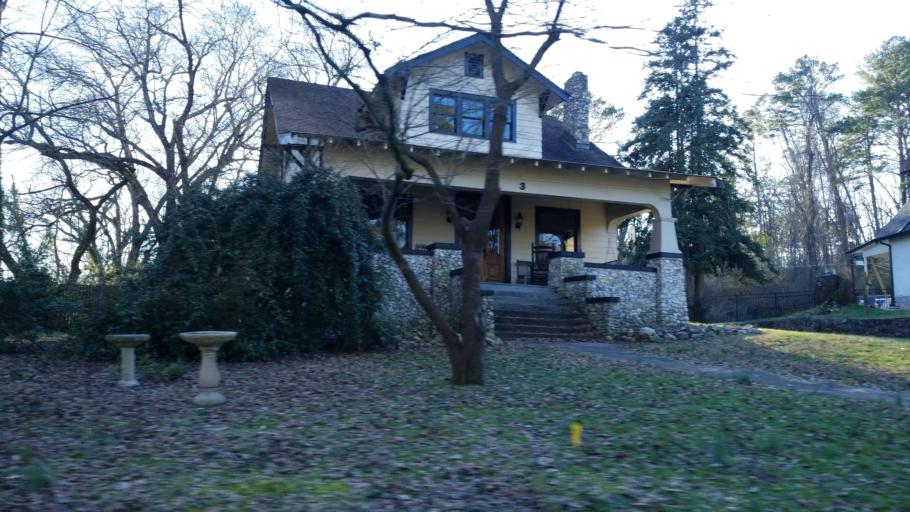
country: US
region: Tennessee
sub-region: Hamilton County
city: East Ridge
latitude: 35.0303
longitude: -85.2469
